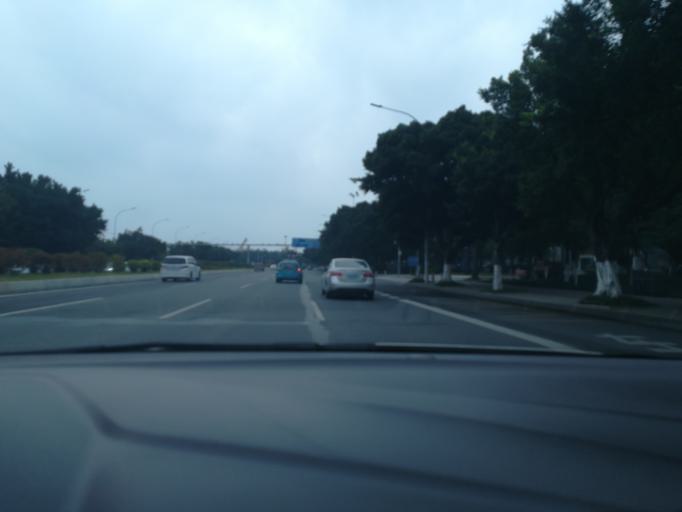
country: CN
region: Guangdong
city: Nansha
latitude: 22.8007
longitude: 113.5794
